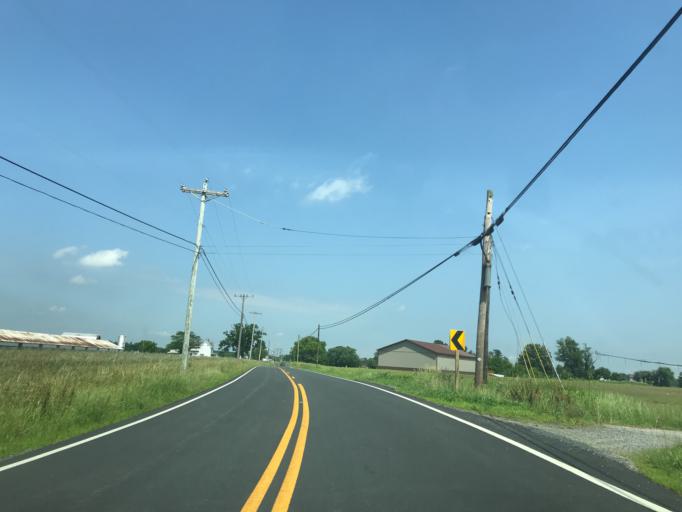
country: US
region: Maryland
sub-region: Dorchester County
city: Hurlock
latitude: 38.5726
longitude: -75.8064
